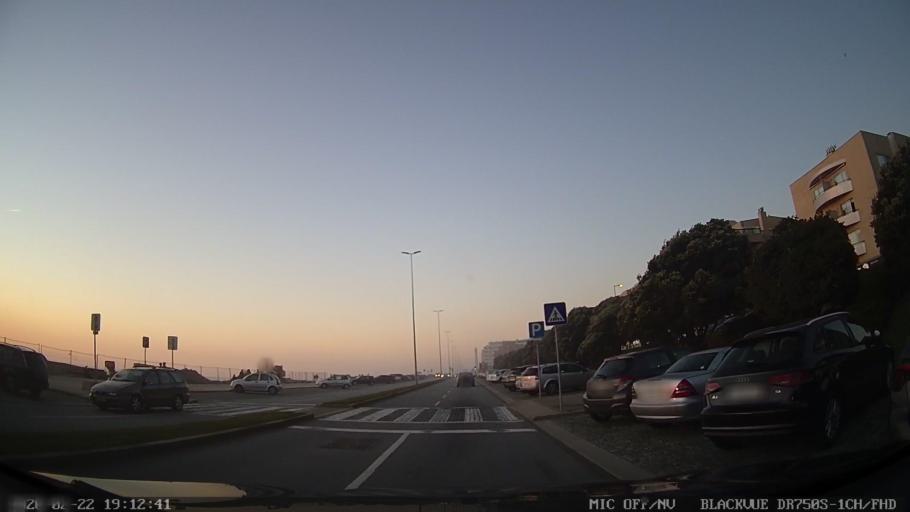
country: PT
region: Porto
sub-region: Matosinhos
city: Leca da Palmeira
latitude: 41.1938
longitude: -8.7072
